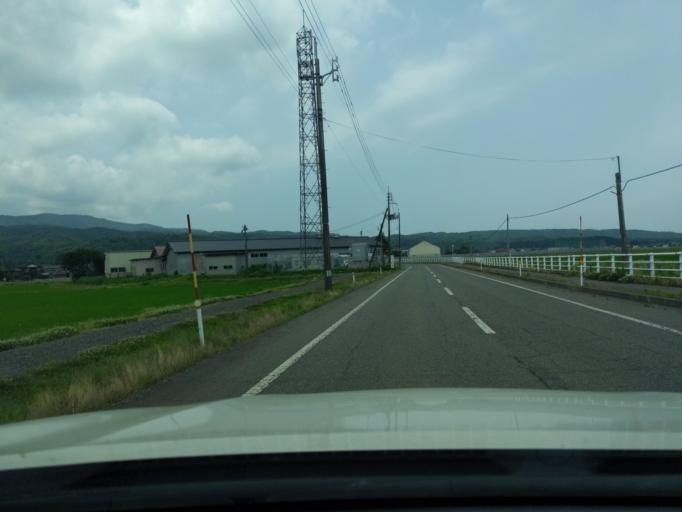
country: JP
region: Niigata
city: Kashiwazaki
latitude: 37.3299
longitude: 138.5722
